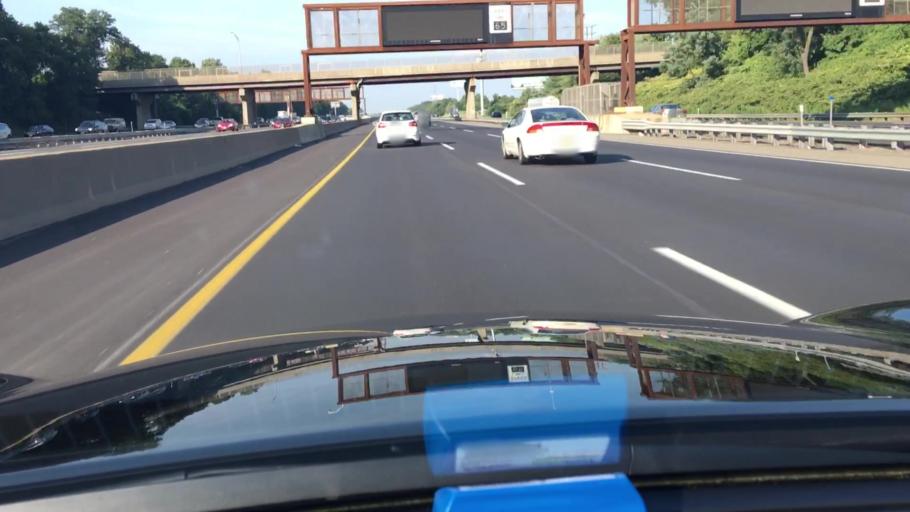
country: US
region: New Jersey
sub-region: Middlesex County
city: Piscataway
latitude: 40.4947
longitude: -74.3880
